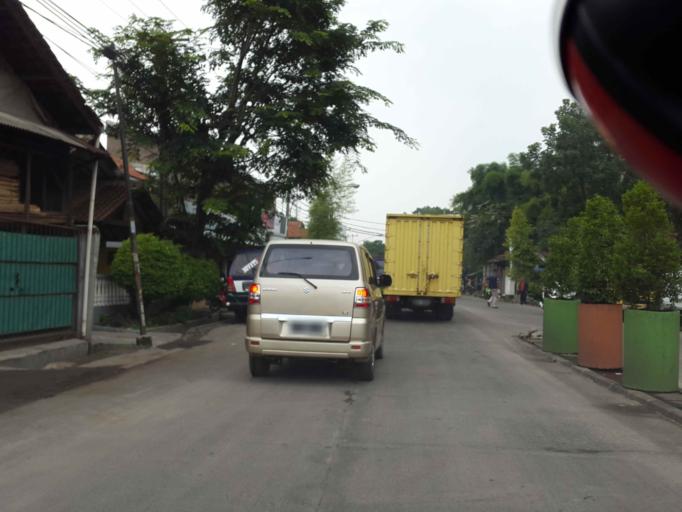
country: ID
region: West Java
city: Cimahi
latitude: -6.9014
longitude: 107.5442
